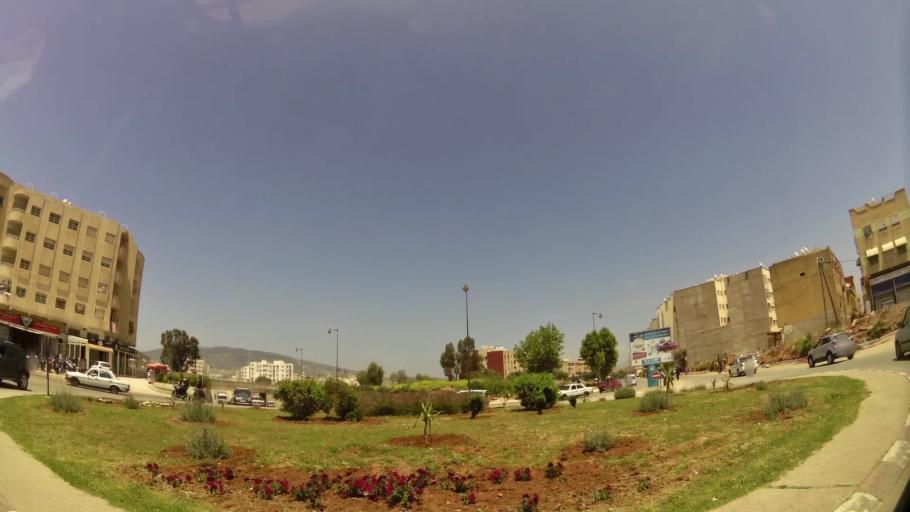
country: MA
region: Fes-Boulemane
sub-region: Fes
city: Fes
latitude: 34.0209
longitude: -5.0388
